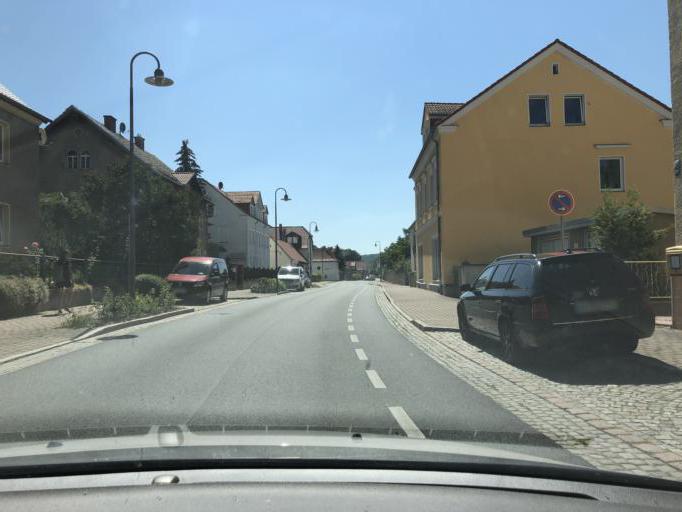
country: DE
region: Saxony
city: Meissen
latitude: 51.1507
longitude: 13.4923
